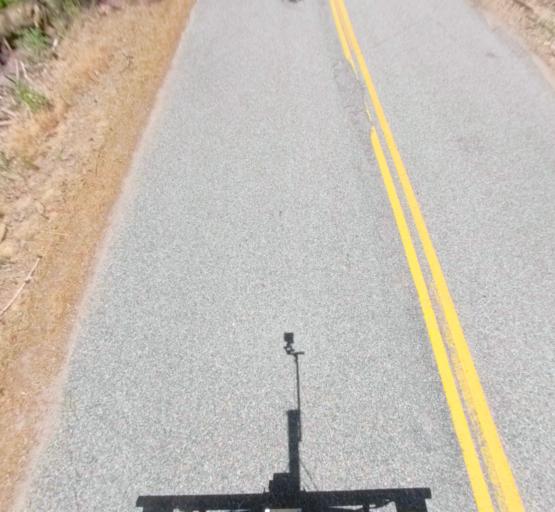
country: US
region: California
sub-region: Madera County
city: Oakhurst
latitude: 37.3660
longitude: -119.5374
